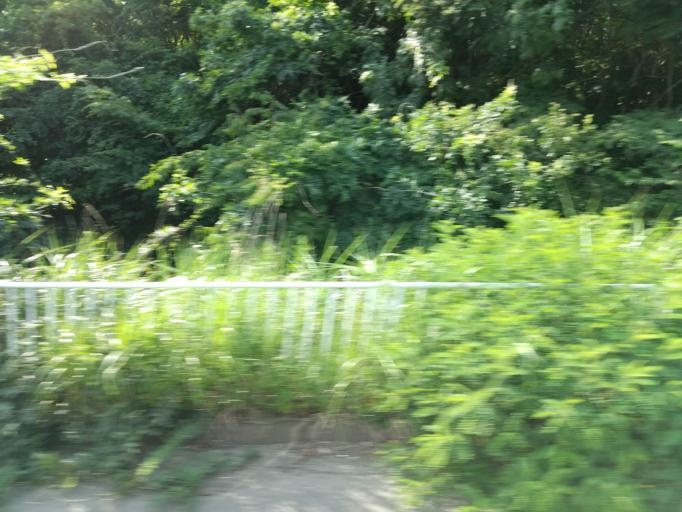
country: JP
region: Miyagi
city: Sendai
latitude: 38.2461
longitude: 140.7382
